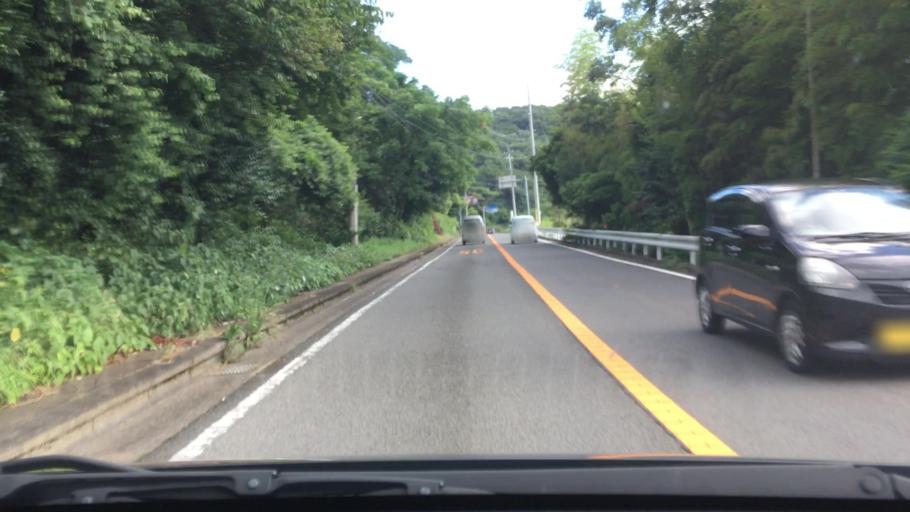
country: JP
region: Nagasaki
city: Togitsu
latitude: 32.8269
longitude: 129.7254
